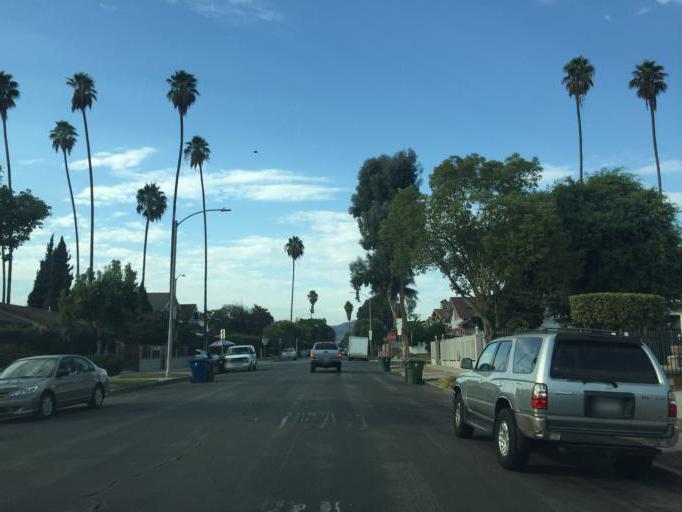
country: US
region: California
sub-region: Los Angeles County
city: Silver Lake
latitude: 34.0706
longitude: -118.3029
